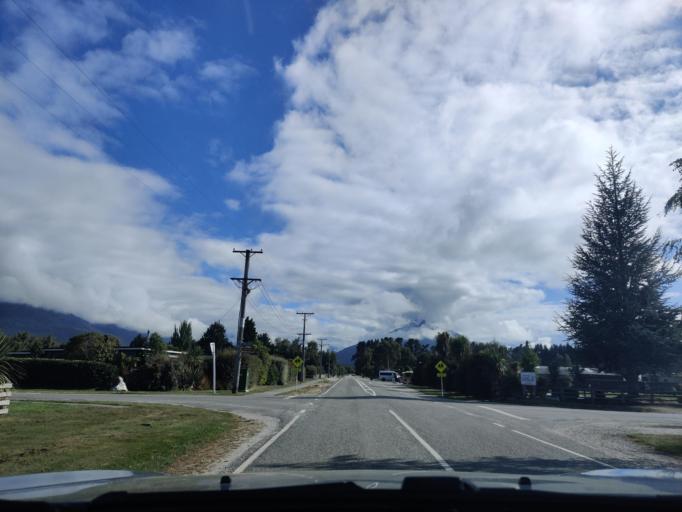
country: NZ
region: Otago
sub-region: Queenstown-Lakes District
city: Queenstown
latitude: -44.8519
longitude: 168.3889
